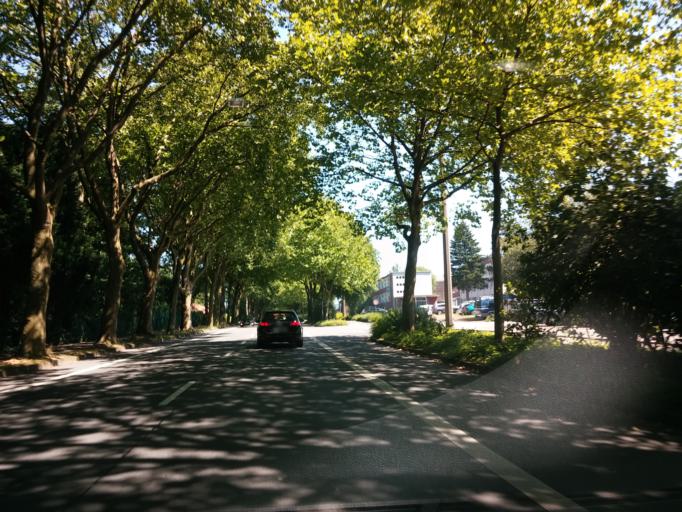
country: DE
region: North Rhine-Westphalia
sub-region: Regierungsbezirk Munster
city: Gladbeck
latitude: 51.5624
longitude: 6.9584
